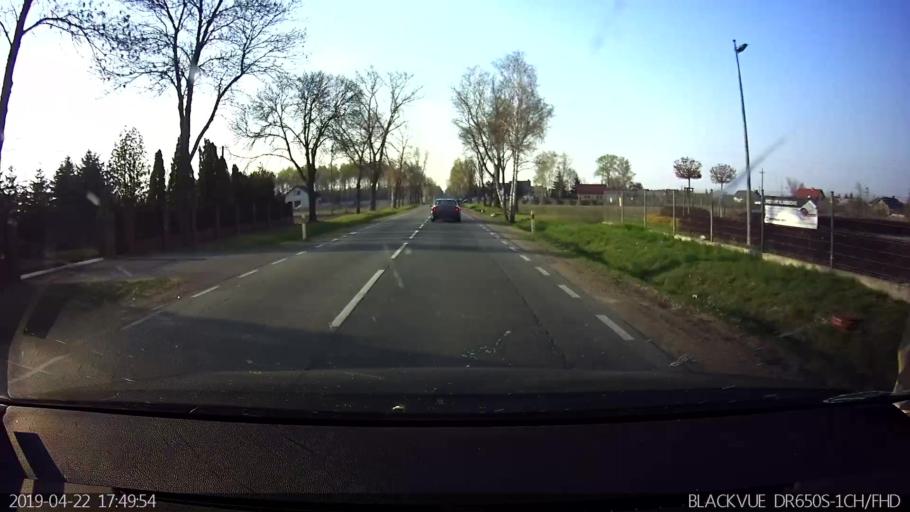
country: PL
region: Masovian Voivodeship
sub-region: Powiat wegrowski
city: Wegrow
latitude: 52.4184
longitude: 22.0058
